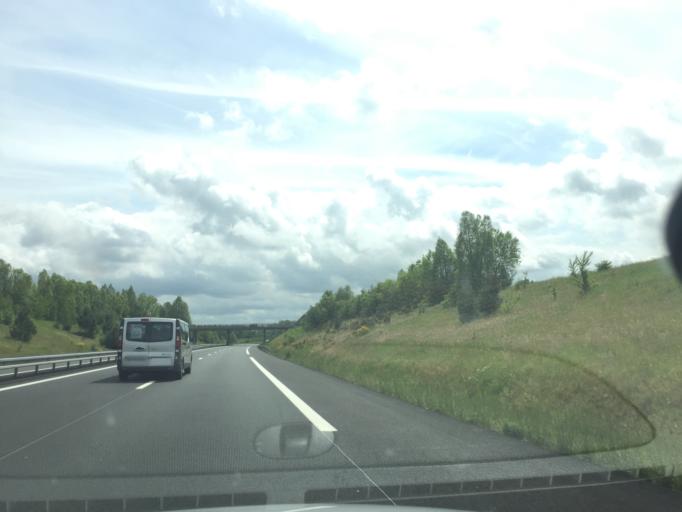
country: FR
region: Pays de la Loire
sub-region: Departement de la Sarthe
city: Marigne-Laille
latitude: 47.8160
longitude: 0.3073
